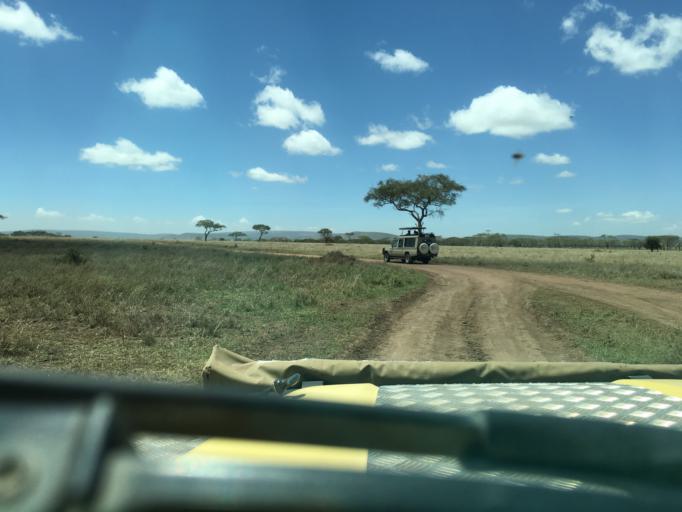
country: TZ
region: Simiyu
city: Kisesa
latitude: -2.6778
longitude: 34.7800
